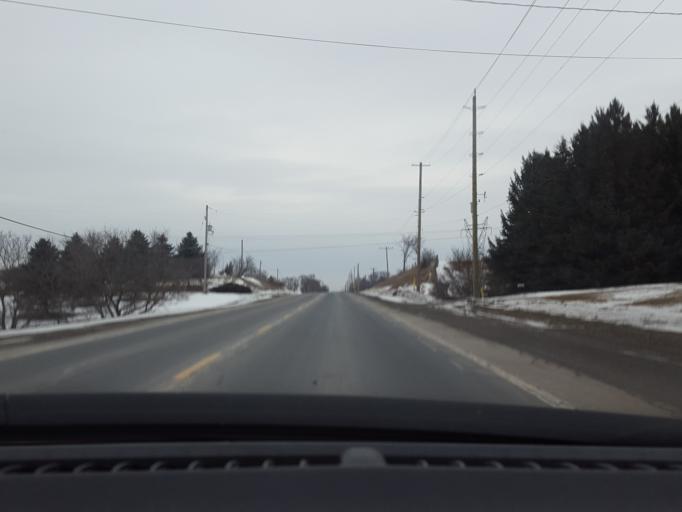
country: CA
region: Ontario
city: Keswick
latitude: 44.1693
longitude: -79.4323
